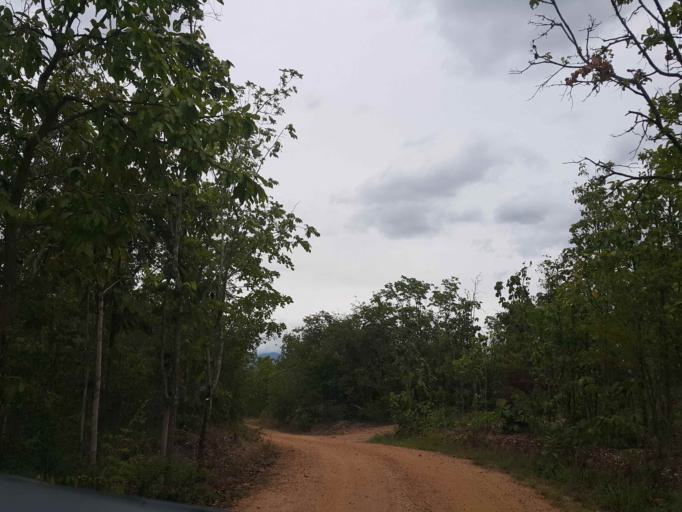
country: TH
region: Chiang Mai
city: Doi Lo
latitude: 18.5040
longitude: 98.7552
